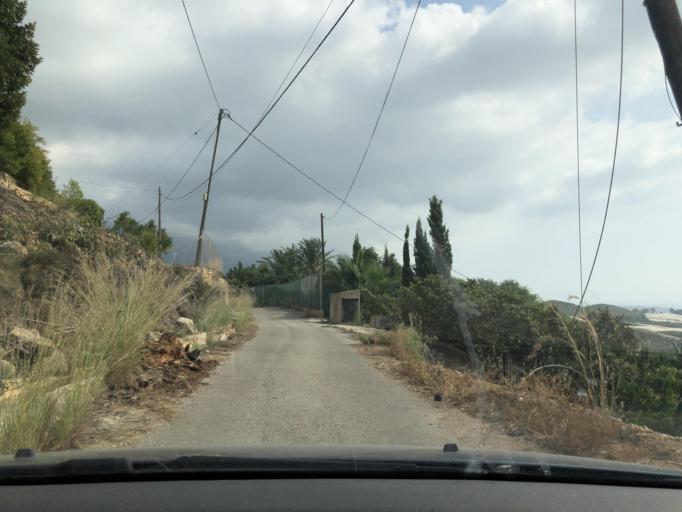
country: ES
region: Valencia
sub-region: Provincia de Alicante
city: Callosa d'En Sarria
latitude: 38.6323
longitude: -0.1078
